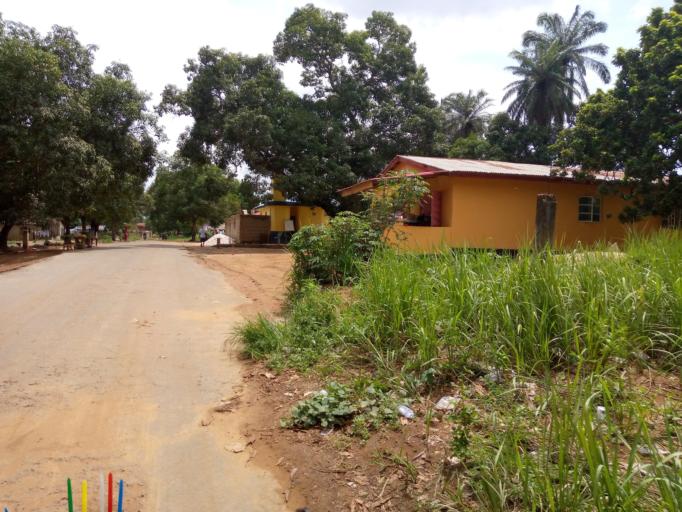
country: SL
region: Western Area
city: Waterloo
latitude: 8.3342
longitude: -13.0134
